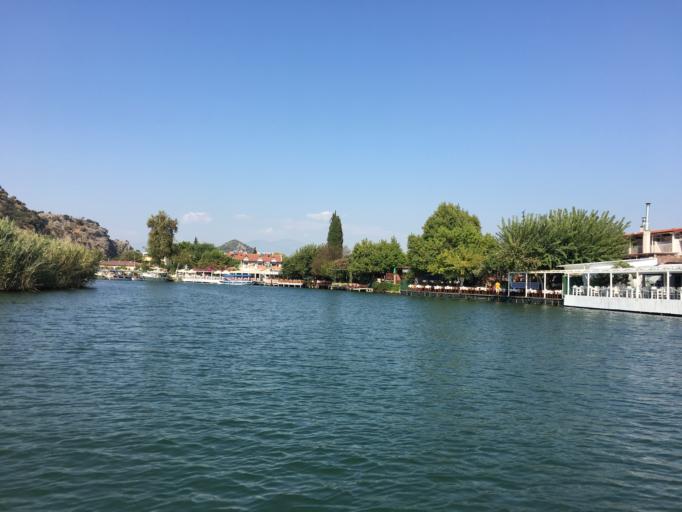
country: TR
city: Dalyan
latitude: 36.8298
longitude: 28.6376
